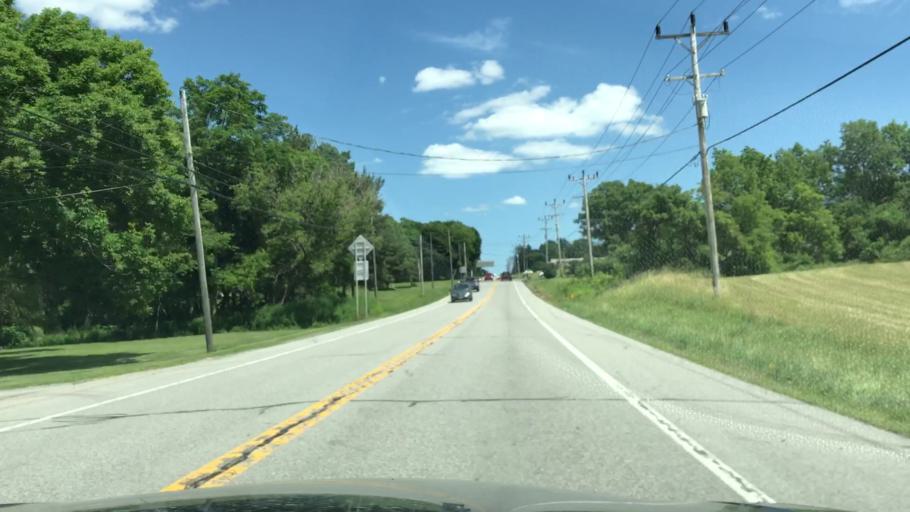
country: US
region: New York
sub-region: Wyoming County
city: Warsaw
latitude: 42.7462
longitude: -78.1166
